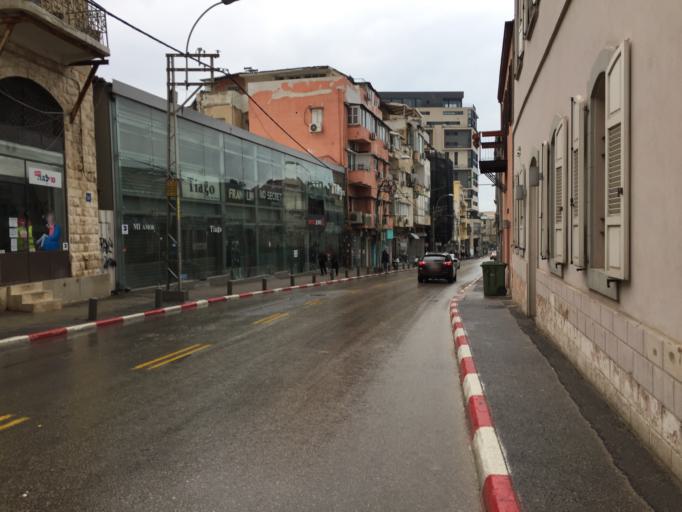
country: IL
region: Tel Aviv
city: Yafo
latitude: 32.0592
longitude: 34.7663
